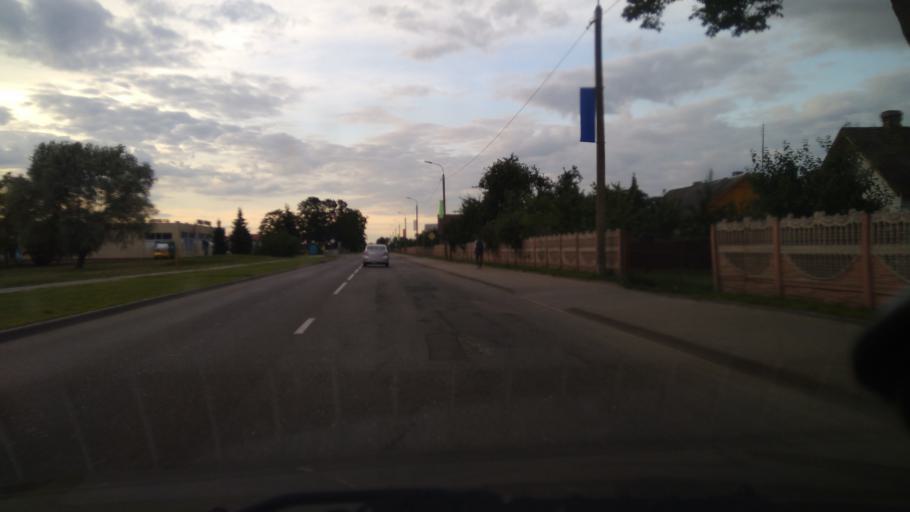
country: BY
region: Grodnenskaya
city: Shchuchin
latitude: 53.5946
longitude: 24.7443
